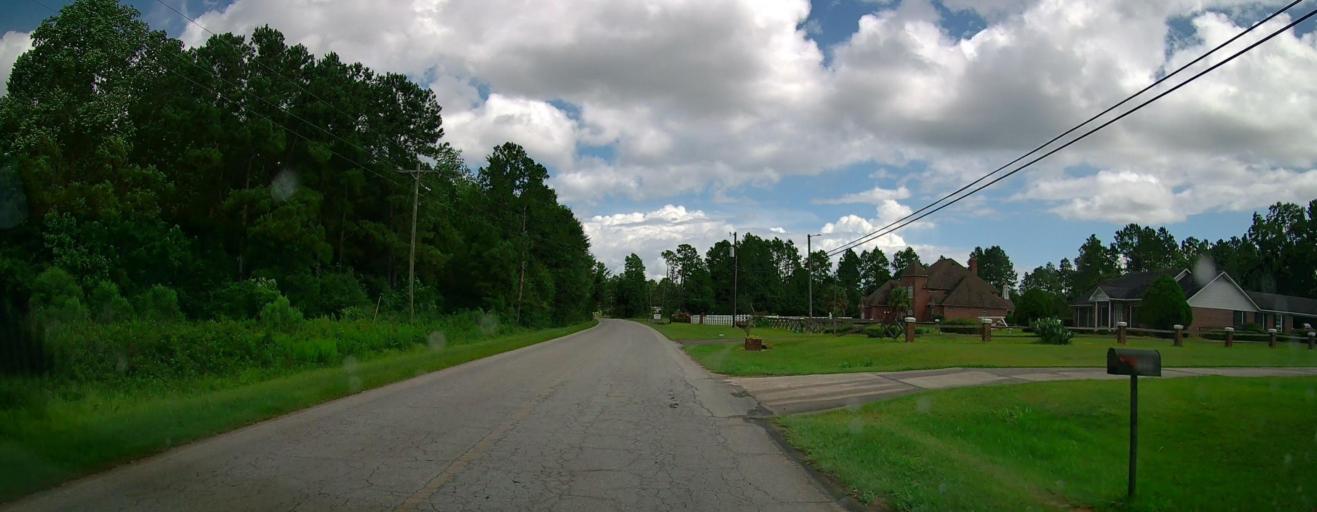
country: US
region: Georgia
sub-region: Ben Hill County
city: Fitzgerald
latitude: 31.7036
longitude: -83.2274
